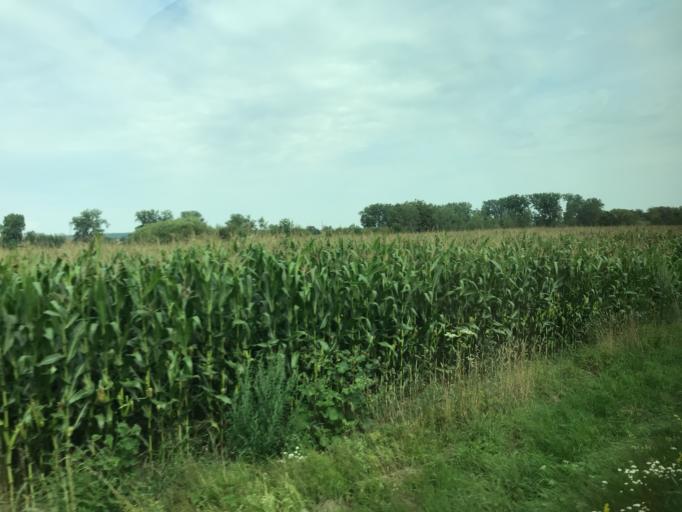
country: CZ
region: Jihocesky
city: Vcelna
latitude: 48.9389
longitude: 14.4639
